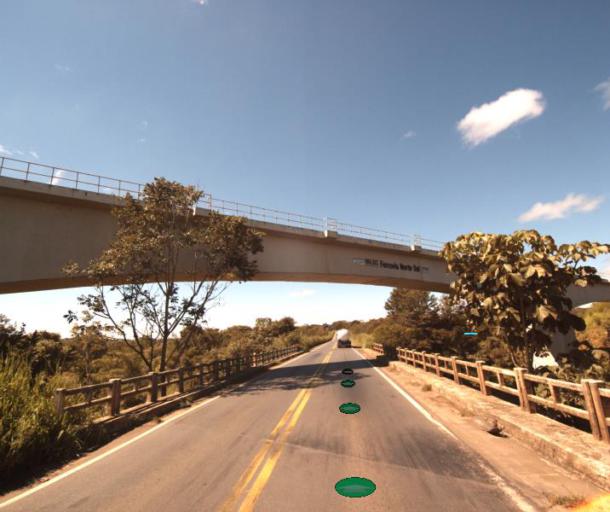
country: BR
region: Goias
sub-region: Jaragua
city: Jaragua
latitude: -15.5496
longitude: -49.4316
